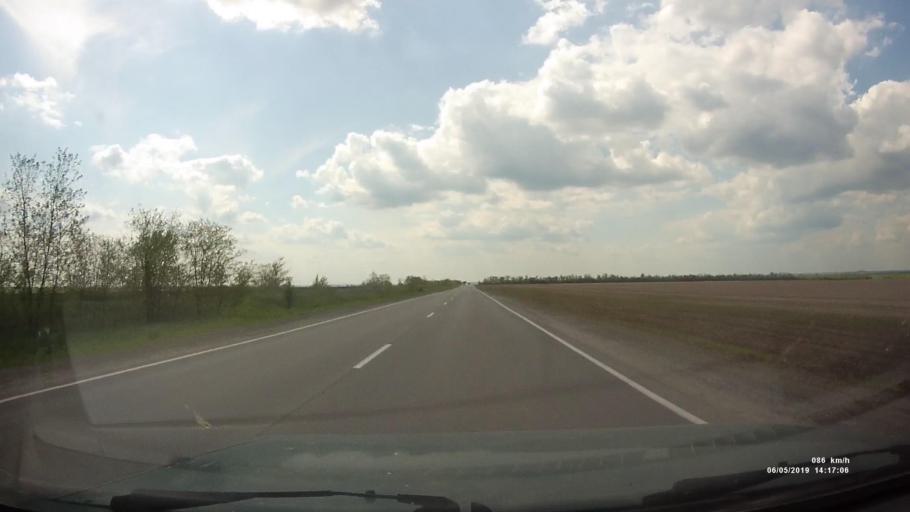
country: RU
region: Rostov
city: Kamenolomni
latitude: 47.6343
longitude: 40.2749
